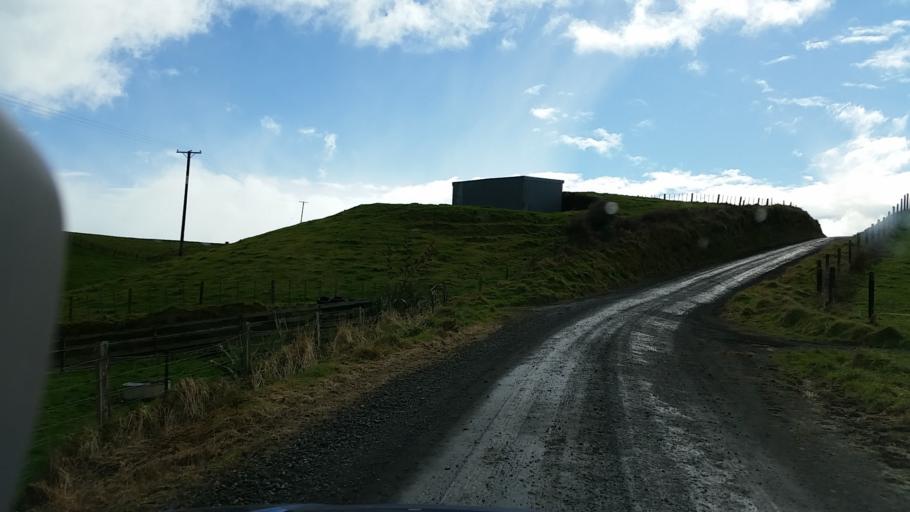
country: NZ
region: Taranaki
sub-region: South Taranaki District
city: Eltham
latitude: -39.2818
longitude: 174.3079
